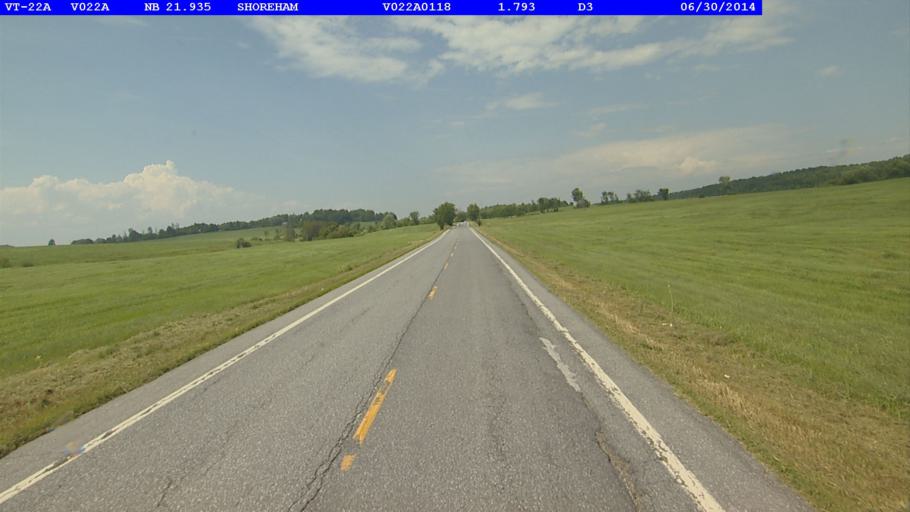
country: US
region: New York
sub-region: Essex County
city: Ticonderoga
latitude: 43.8753
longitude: -73.3096
